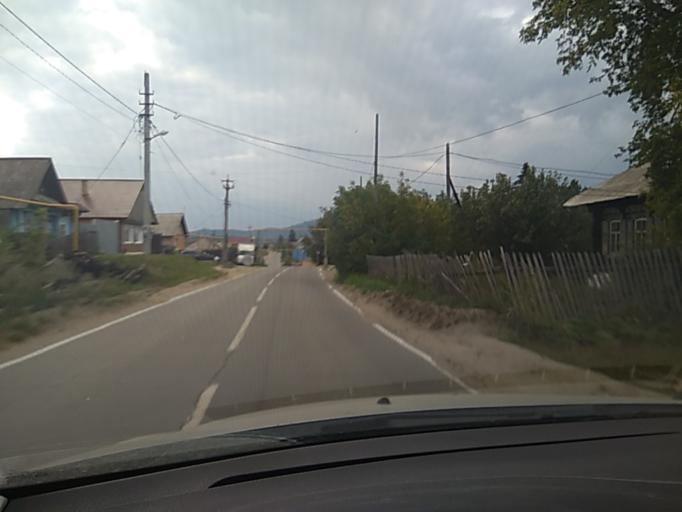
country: RU
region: Chelyabinsk
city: Kyshtym
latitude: 55.6981
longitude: 60.5400
